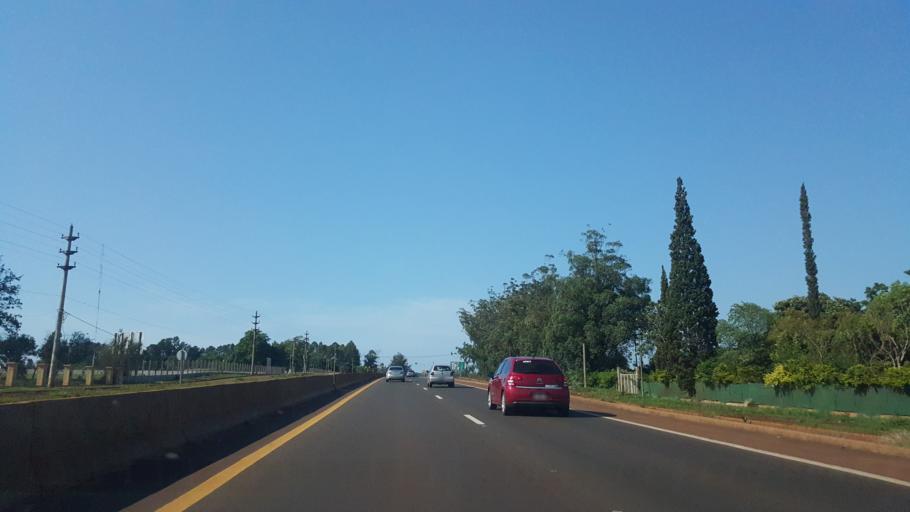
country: AR
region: Misiones
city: Garupa
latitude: -27.4761
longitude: -55.8634
